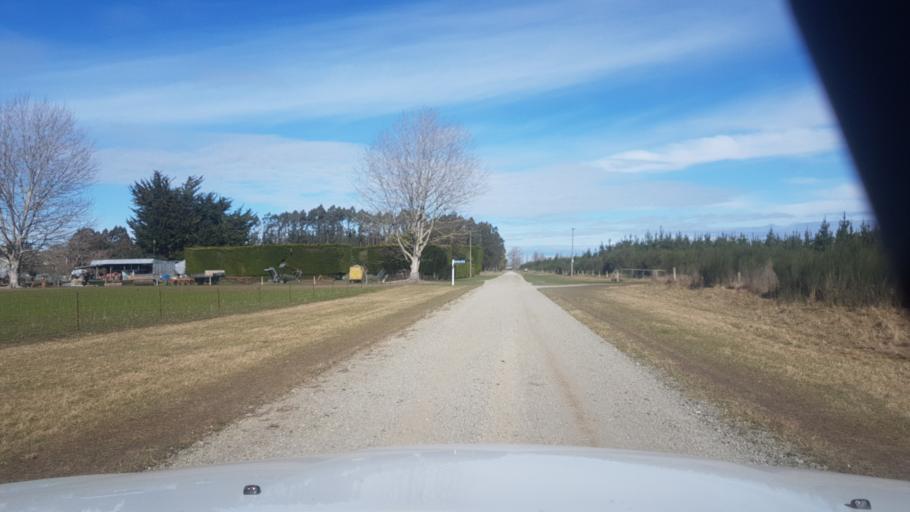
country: NZ
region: Canterbury
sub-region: Timaru District
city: Pleasant Point
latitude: -44.1365
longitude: 171.2772
